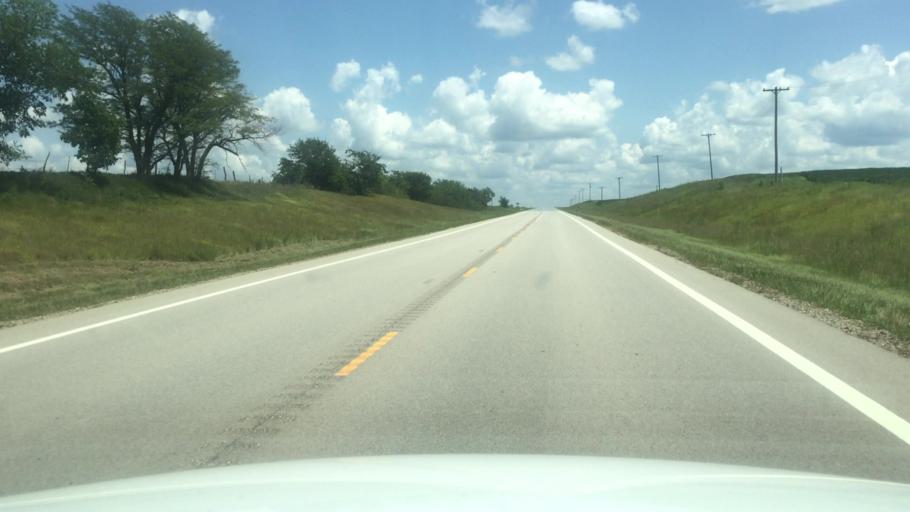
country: US
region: Kansas
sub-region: Brown County
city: Horton
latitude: 39.6673
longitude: -95.4493
